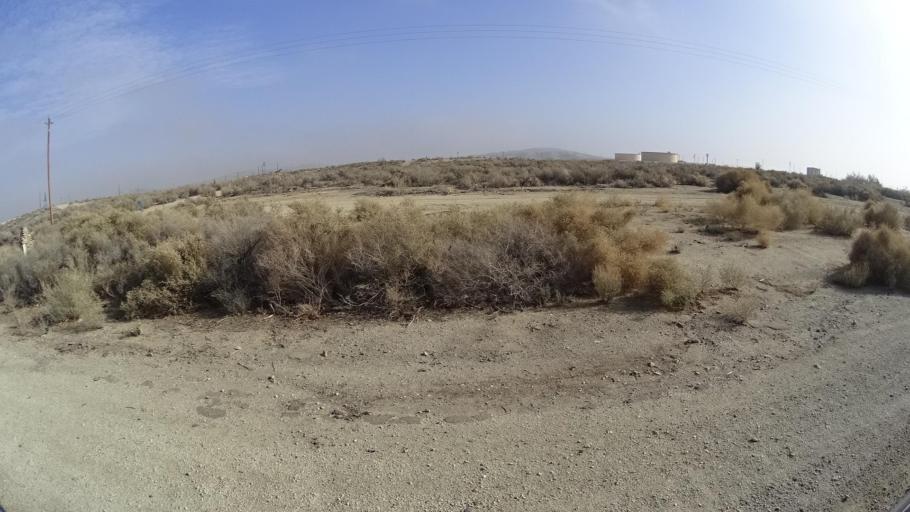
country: US
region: California
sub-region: Kern County
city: Ford City
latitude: 35.1702
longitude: -119.4652
